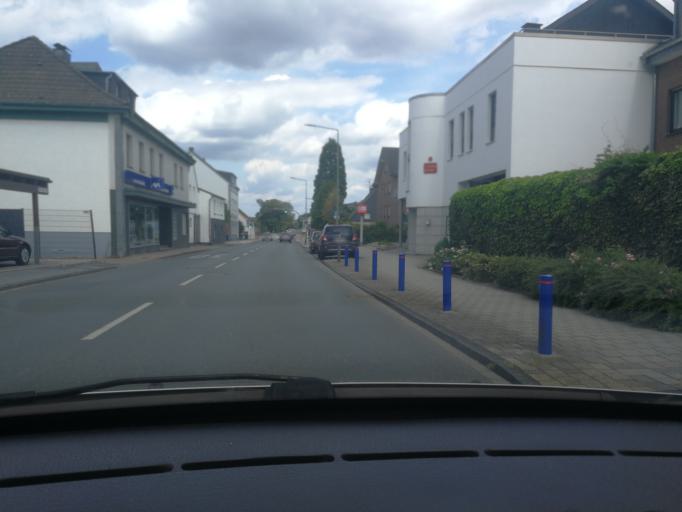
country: DE
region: North Rhine-Westphalia
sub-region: Regierungsbezirk Dusseldorf
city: Moers
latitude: 51.3940
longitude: 6.6570
